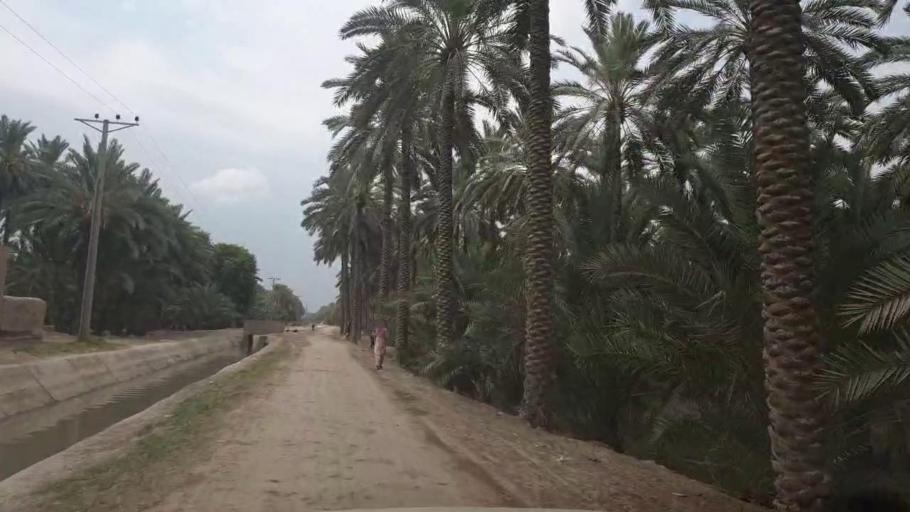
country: PK
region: Sindh
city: Khairpur
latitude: 27.6151
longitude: 68.8052
